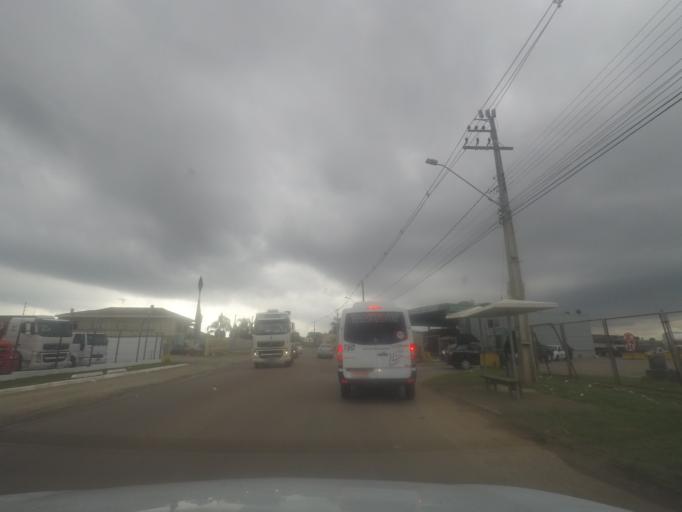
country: BR
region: Parana
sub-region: Sao Jose Dos Pinhais
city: Sao Jose dos Pinhais
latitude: -25.5594
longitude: -49.2694
